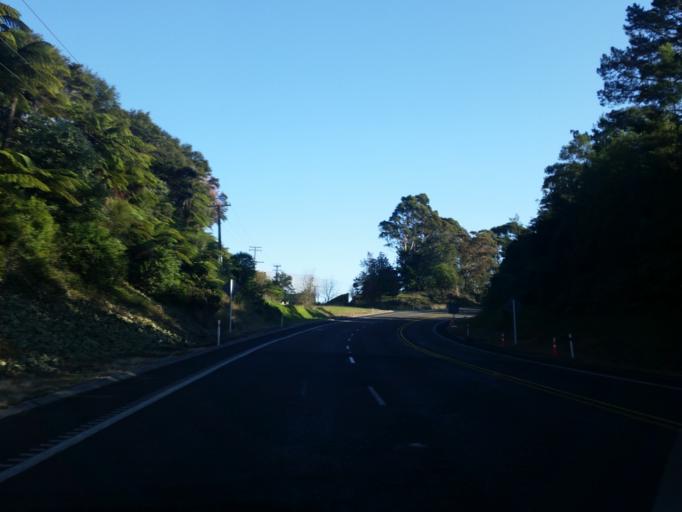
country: NZ
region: Bay of Plenty
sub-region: Western Bay of Plenty District
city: Katikati
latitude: -37.6334
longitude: 175.9584
